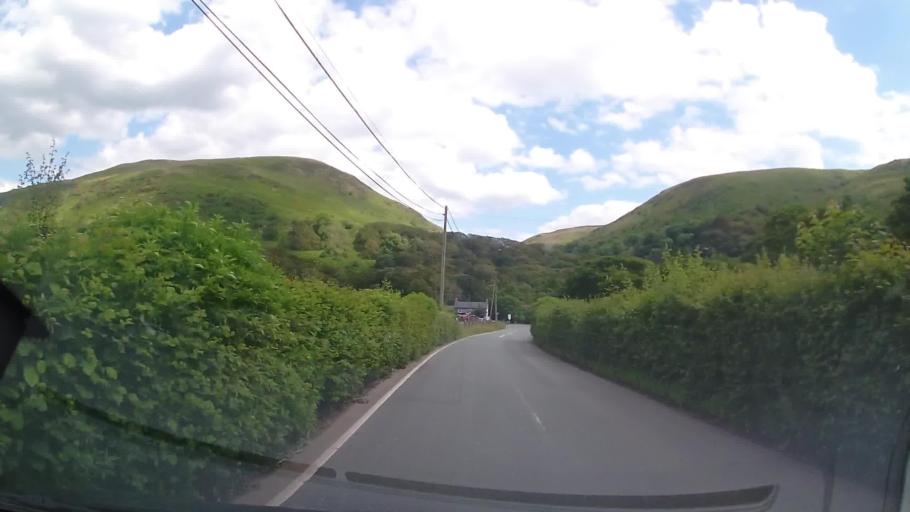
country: GB
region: Wales
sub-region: Gwynedd
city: Tywyn
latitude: 52.6235
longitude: -3.9984
